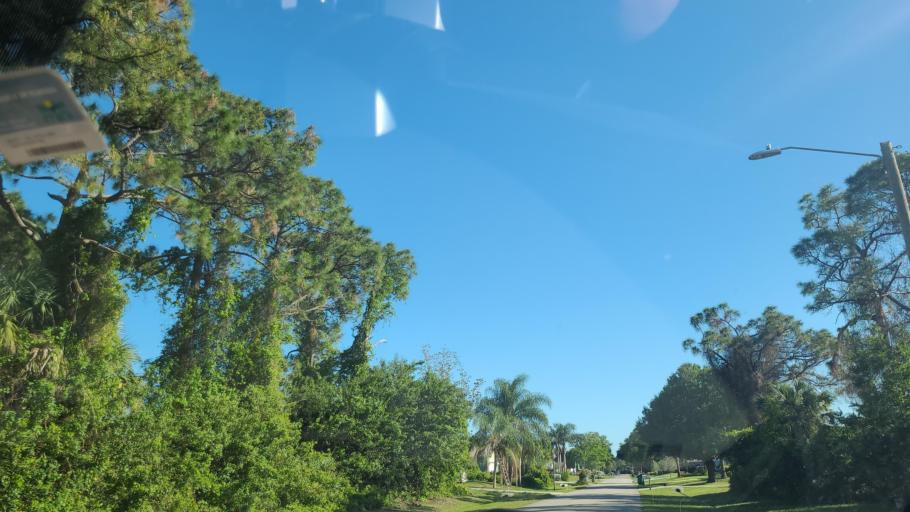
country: US
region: Florida
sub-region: Indian River County
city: Sebastian
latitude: 27.8045
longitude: -80.4912
